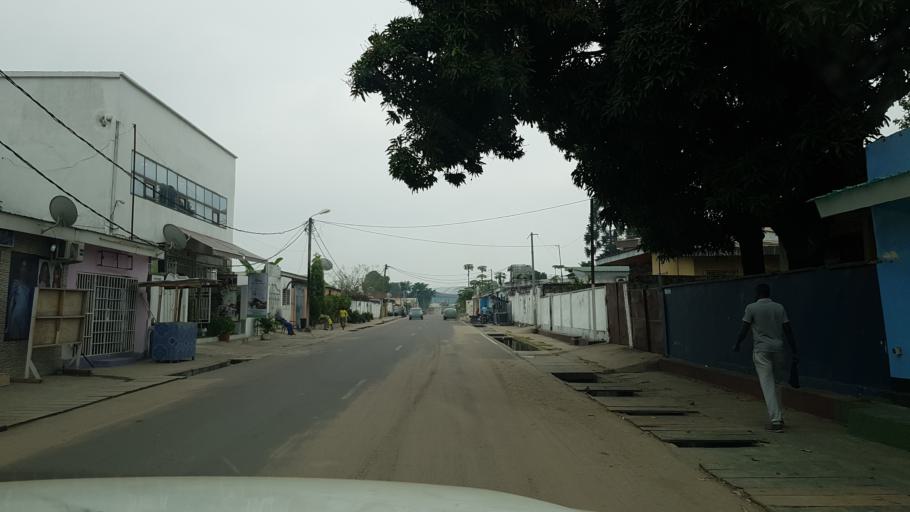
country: CG
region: Brazzaville
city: Brazzaville
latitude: -4.2581
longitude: 15.2588
